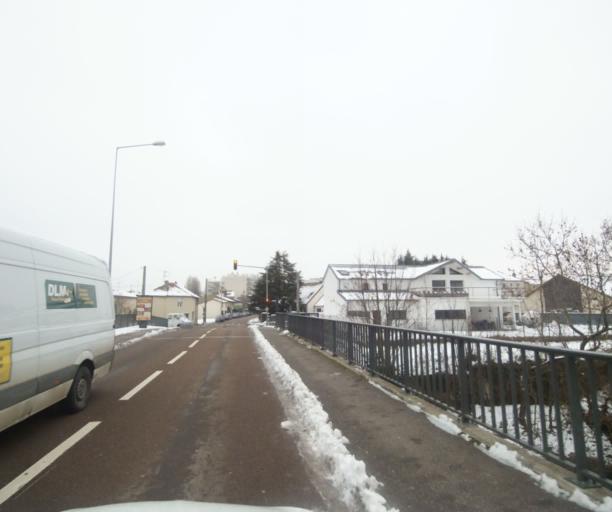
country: FR
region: Champagne-Ardenne
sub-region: Departement de la Haute-Marne
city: Saint-Dizier
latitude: 48.6345
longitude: 4.9385
